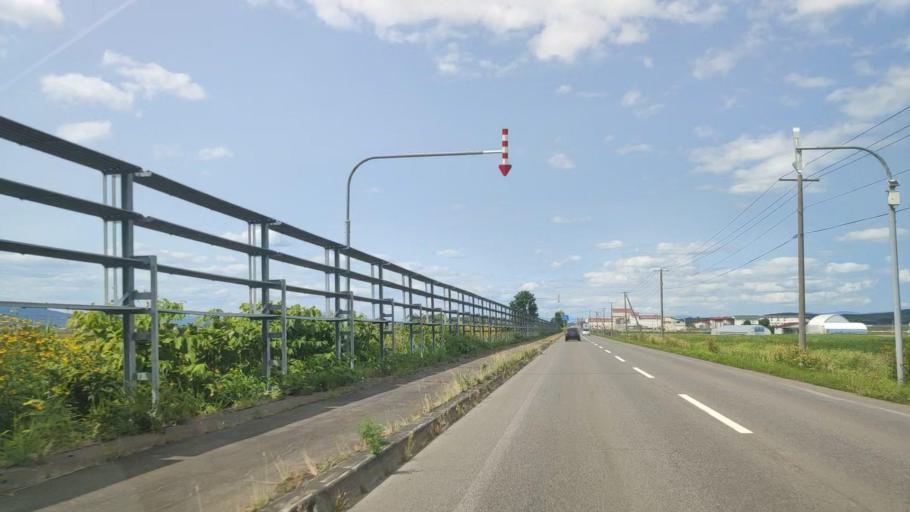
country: JP
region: Hokkaido
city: Nayoro
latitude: 44.1976
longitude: 142.4159
